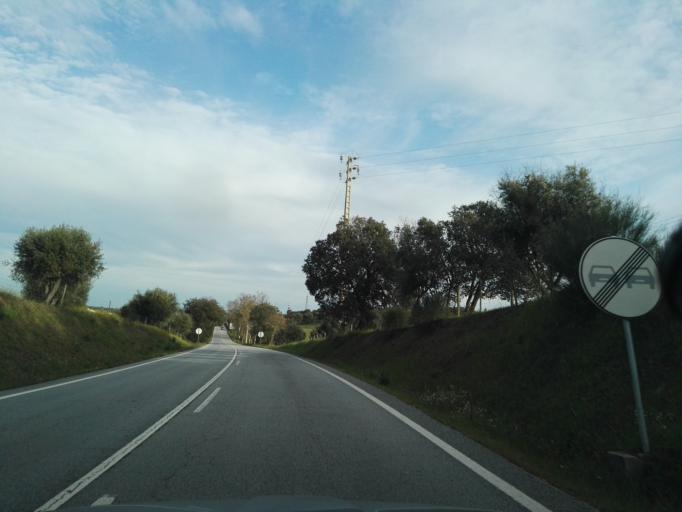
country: PT
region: Portalegre
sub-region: Arronches
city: Arronches
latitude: 39.1185
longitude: -7.2935
